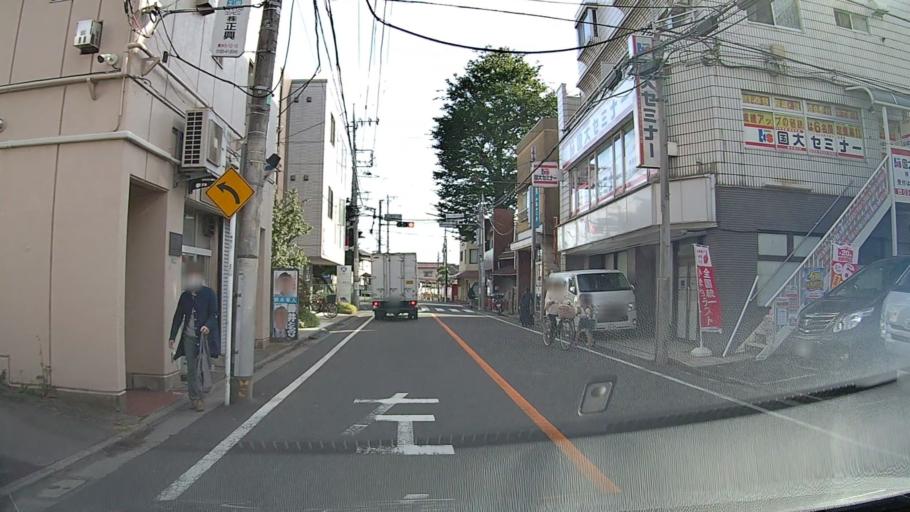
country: JP
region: Saitama
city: Wako
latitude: 35.7499
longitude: 139.6402
